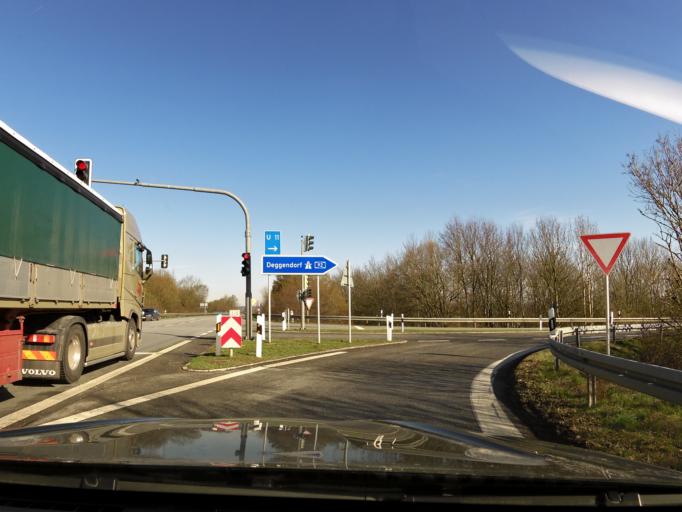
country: DE
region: Bavaria
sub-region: Upper Bavaria
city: Marzling
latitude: 48.3860
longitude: 11.7800
